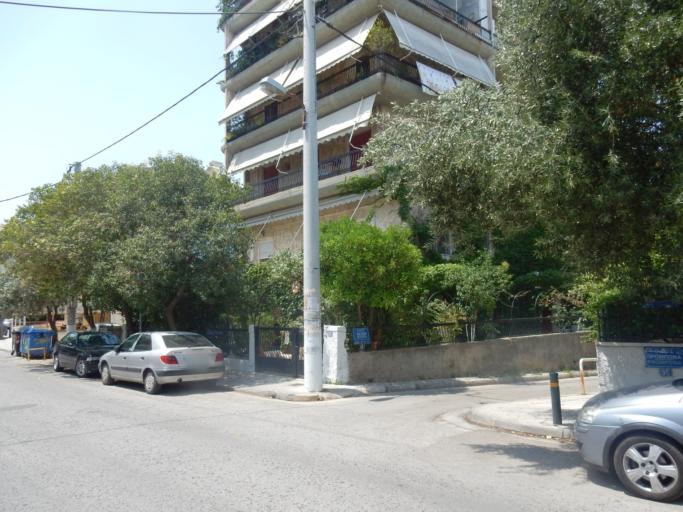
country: GR
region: Attica
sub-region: Nomarchia Athinas
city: Nea Filadelfeia
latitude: 38.0282
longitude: 23.7382
